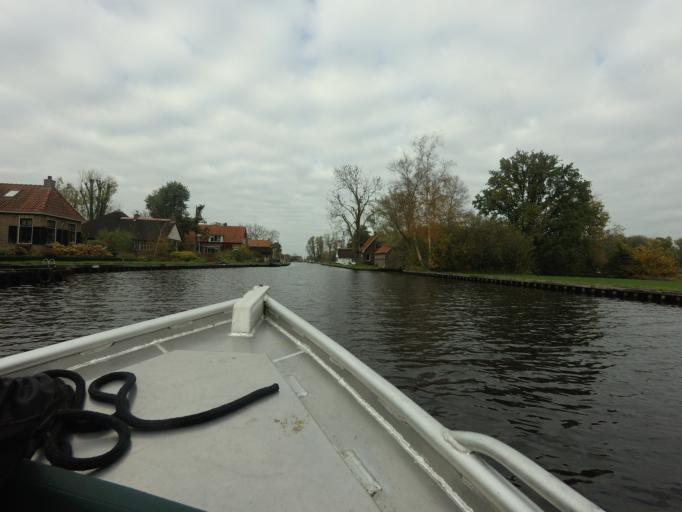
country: NL
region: Overijssel
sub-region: Gemeente Steenwijkerland
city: Oldemarkt
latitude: 52.8049
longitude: 5.9241
